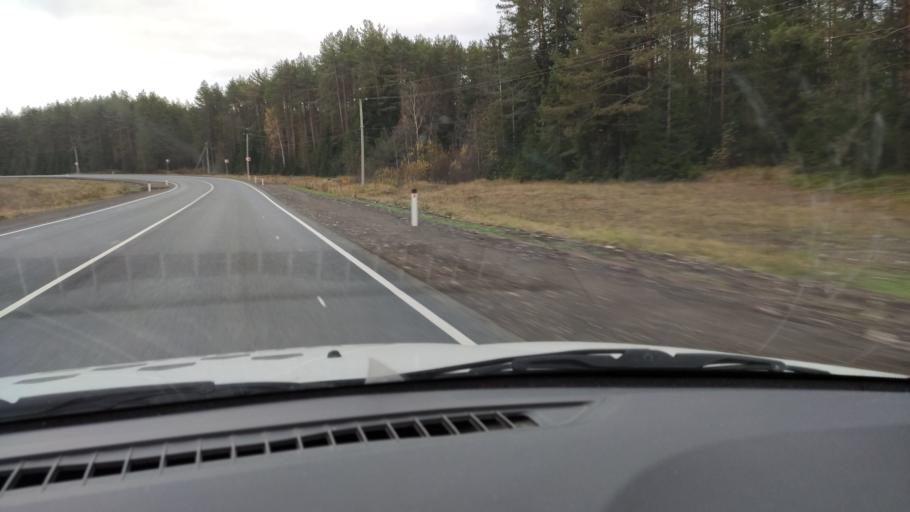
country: RU
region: Kirov
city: Belaya Kholunitsa
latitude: 58.8408
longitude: 50.7784
